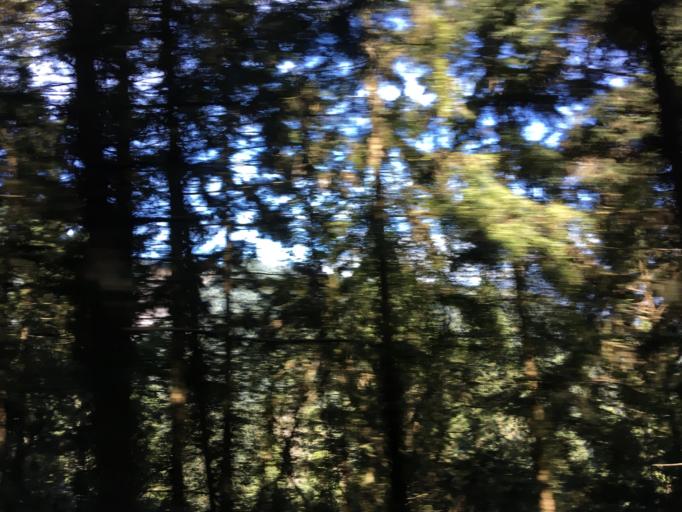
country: TW
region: Taiwan
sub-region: Yilan
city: Yilan
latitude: 24.5429
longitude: 121.5112
